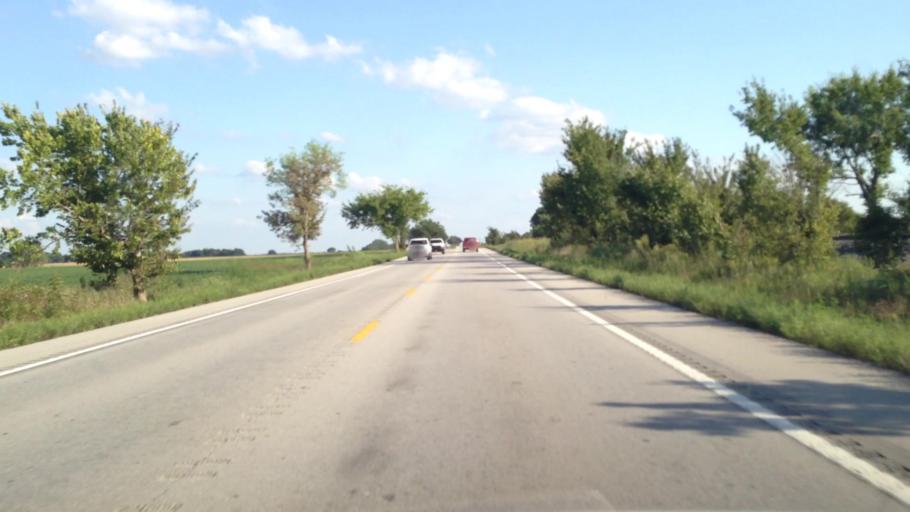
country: US
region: Missouri
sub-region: Jasper County
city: Carl Junction
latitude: 37.2689
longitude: -94.5985
